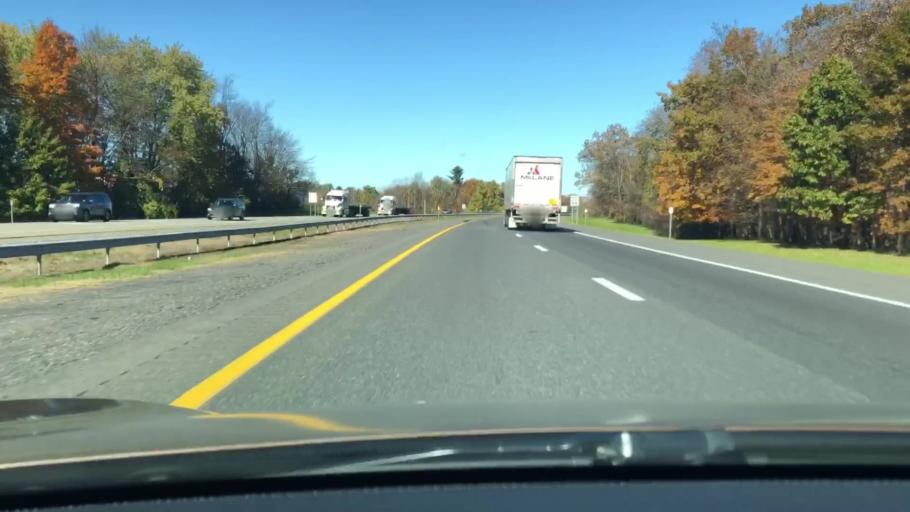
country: US
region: New York
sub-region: Ulster County
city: Plattekill
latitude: 41.5836
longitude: -74.0885
